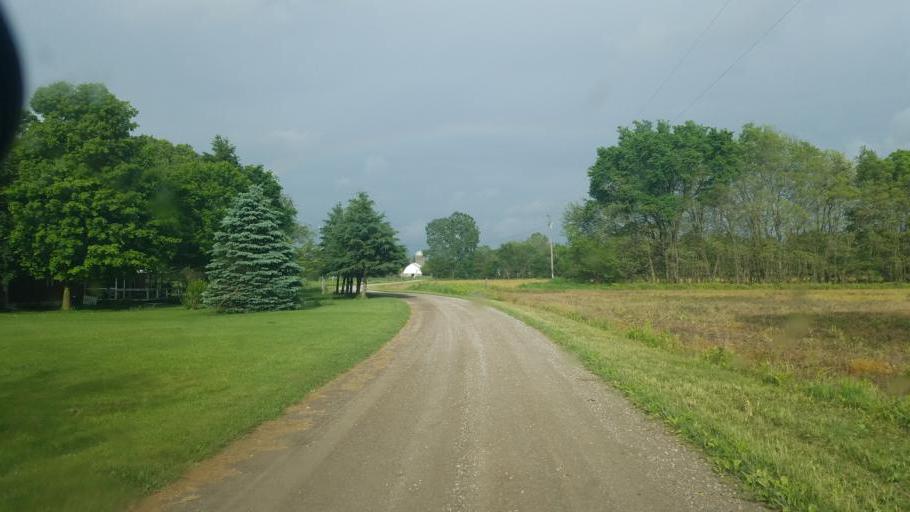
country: US
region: Ohio
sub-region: Knox County
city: Fredericktown
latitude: 40.5113
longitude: -82.6503
